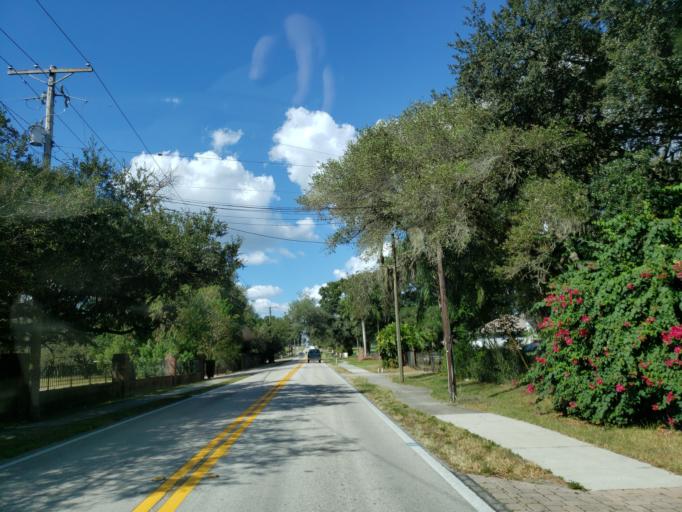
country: US
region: Florida
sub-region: Hillsborough County
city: Bloomingdale
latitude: 27.9028
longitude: -82.2441
